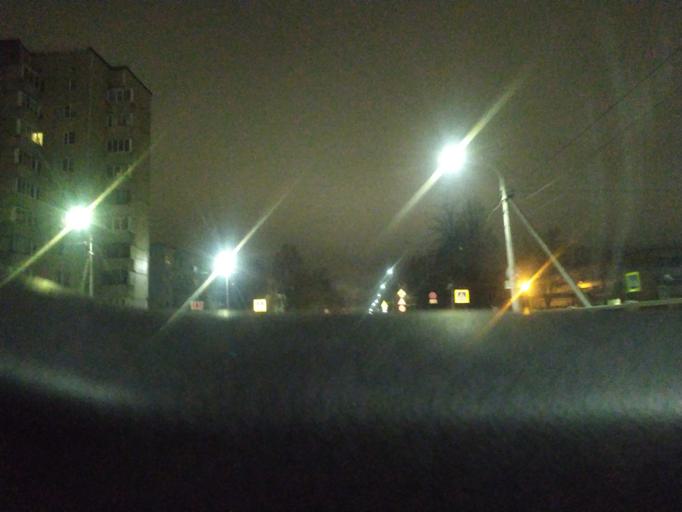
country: RU
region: Leningrad
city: Kirovsk
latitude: 59.8795
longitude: 30.9971
